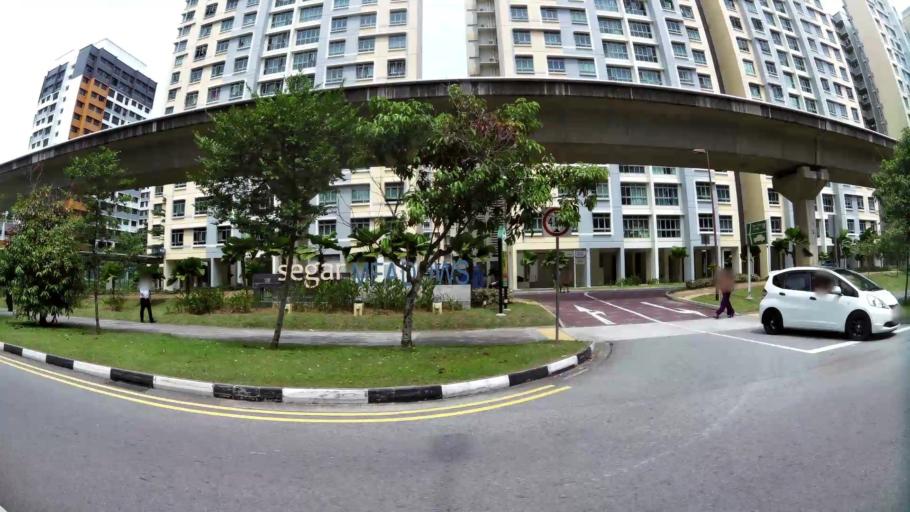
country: MY
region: Johor
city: Johor Bahru
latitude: 1.3872
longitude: 103.7704
